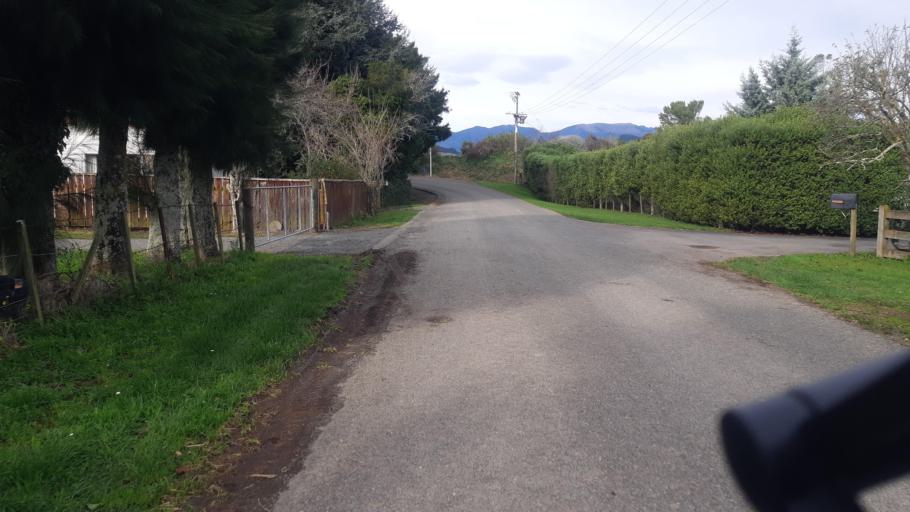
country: NZ
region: Tasman
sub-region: Tasman District
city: Brightwater
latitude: -41.3578
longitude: 173.1204
